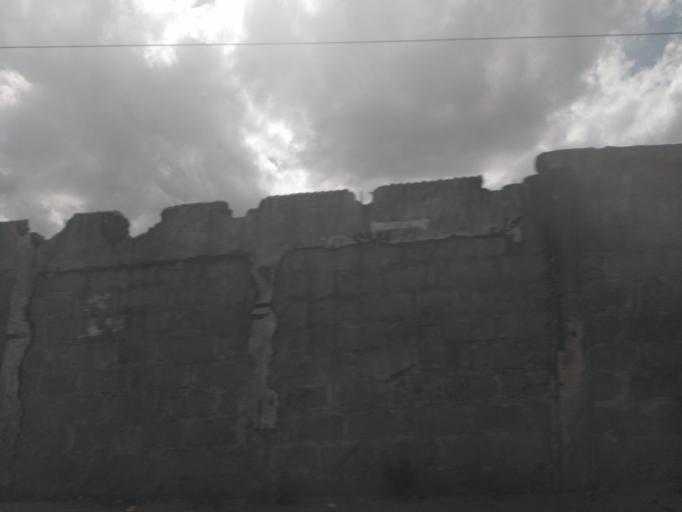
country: TZ
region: Dar es Salaam
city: Dar es Salaam
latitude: -6.8688
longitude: 39.2559
